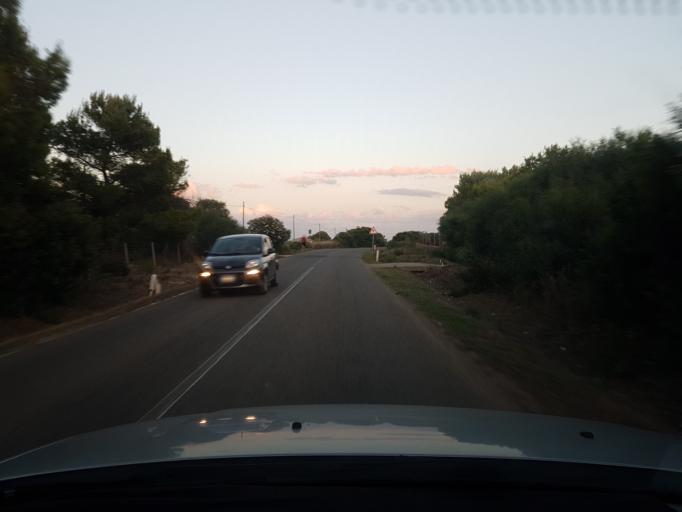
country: IT
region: Sardinia
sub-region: Provincia di Oristano
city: Riola Sardo
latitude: 40.0273
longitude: 8.4270
